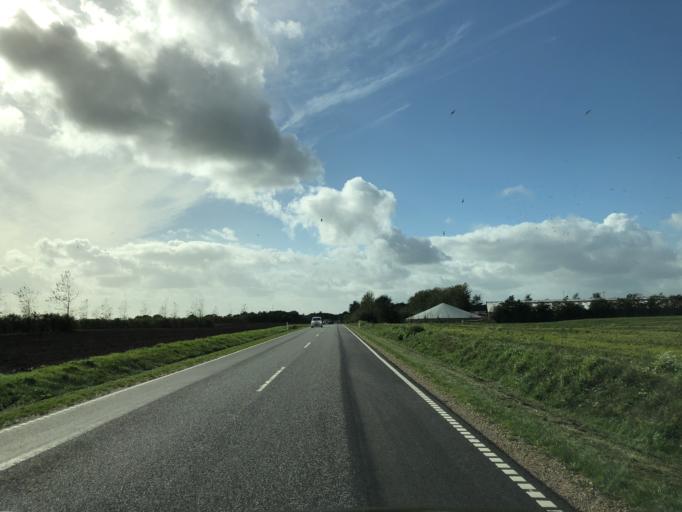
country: DK
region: Central Jutland
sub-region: Holstebro Kommune
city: Holstebro
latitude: 56.3678
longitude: 8.4566
